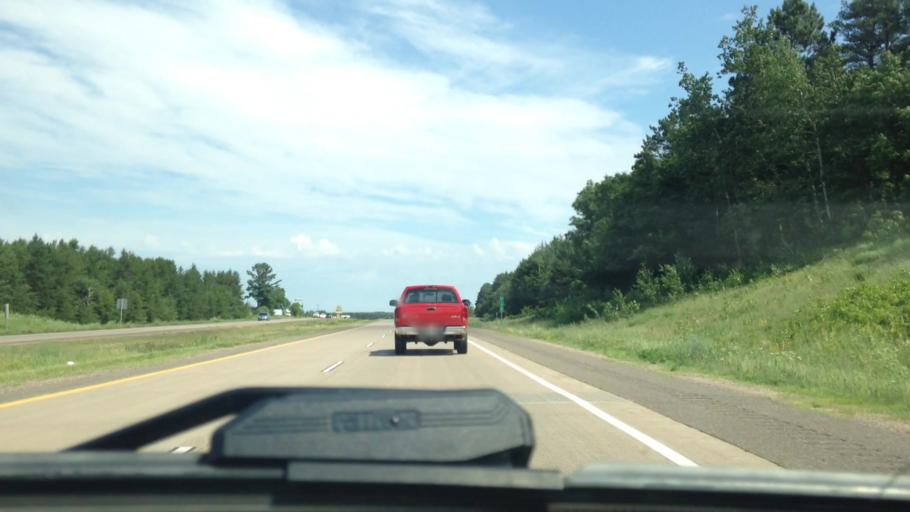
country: US
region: Wisconsin
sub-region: Washburn County
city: Spooner
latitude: 45.8939
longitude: -91.8275
